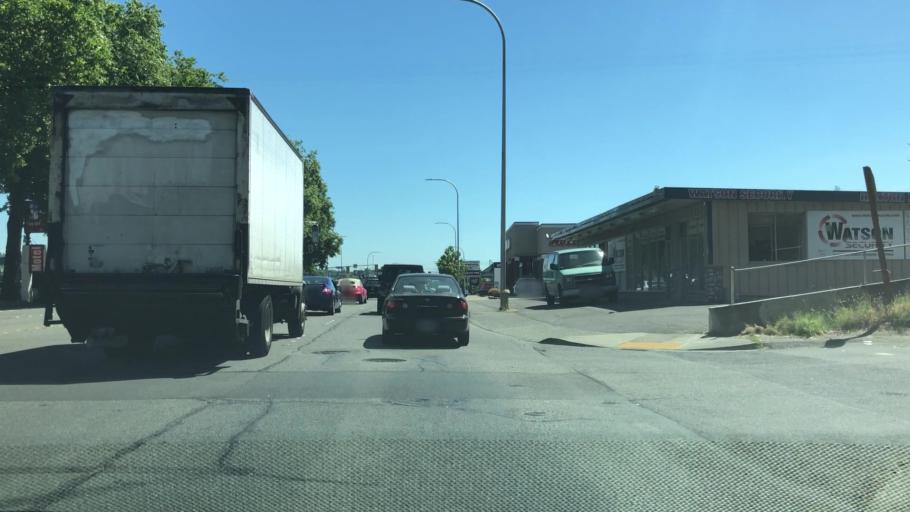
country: US
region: Washington
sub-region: King County
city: Renton
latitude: 47.4830
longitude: -122.2173
